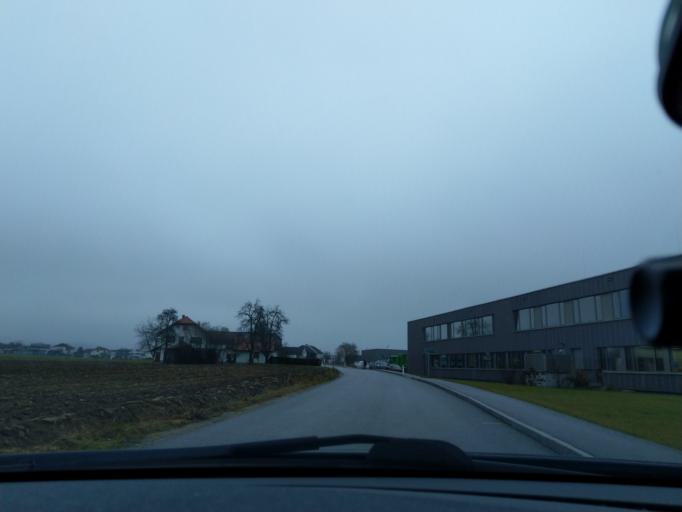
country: AT
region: Upper Austria
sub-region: Politischer Bezirk Urfahr-Umgebung
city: Engerwitzdorf
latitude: 48.3751
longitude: 14.5147
